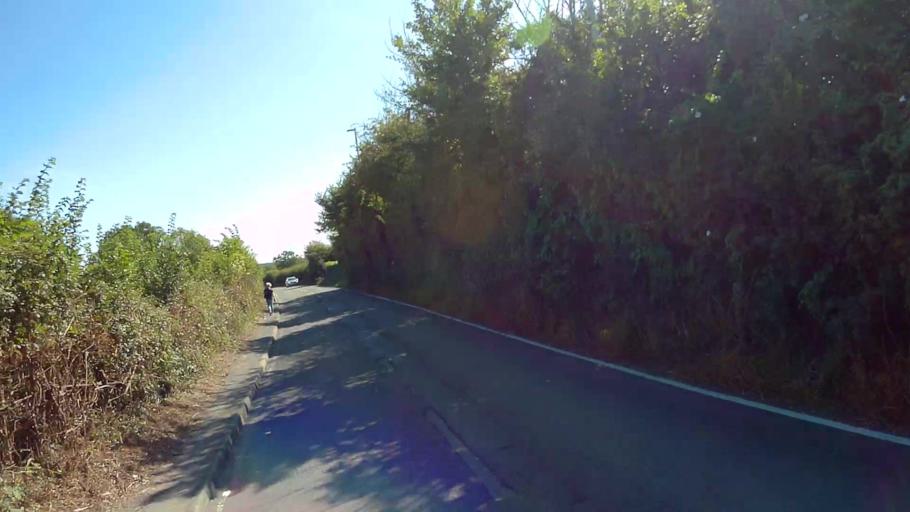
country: GB
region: England
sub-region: Wokingham
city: Swallowfield
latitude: 51.3847
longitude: -0.9719
